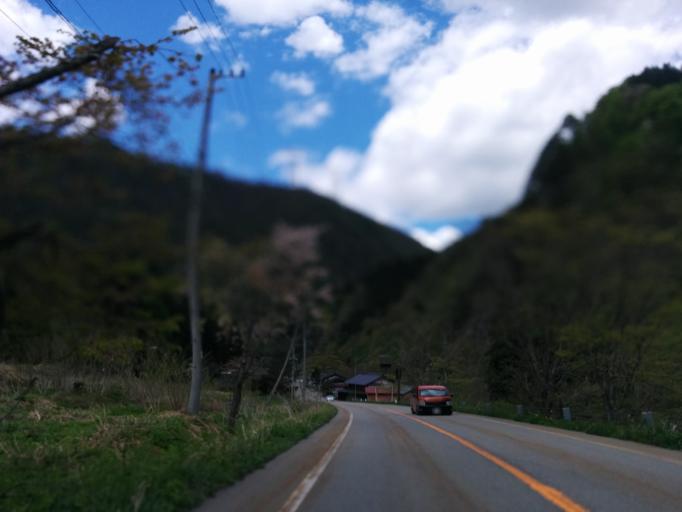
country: JP
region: Toyama
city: Fukumitsu
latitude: 36.3210
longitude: 136.8977
